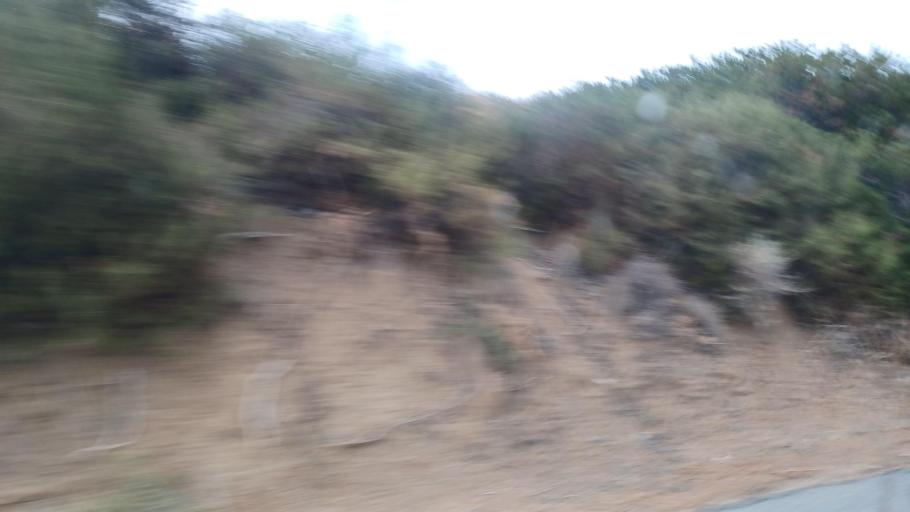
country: CY
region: Pafos
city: Polis
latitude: 35.0307
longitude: 32.4654
